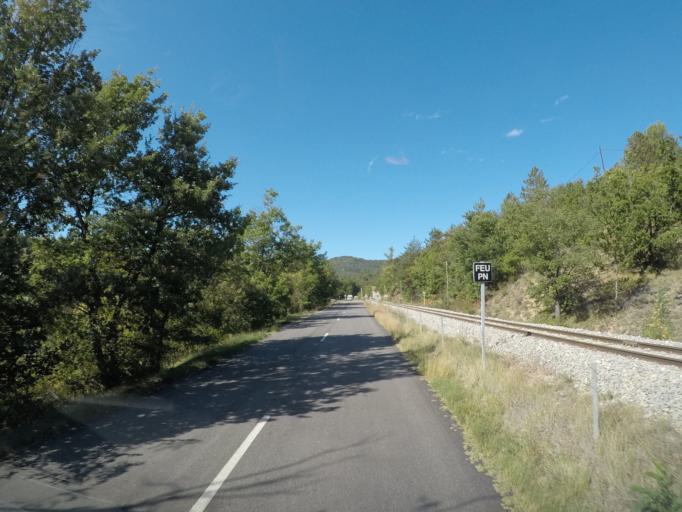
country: FR
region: Provence-Alpes-Cote d'Azur
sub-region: Departement des Alpes-de-Haute-Provence
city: Mallemoisson
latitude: 44.0107
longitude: 6.1910
